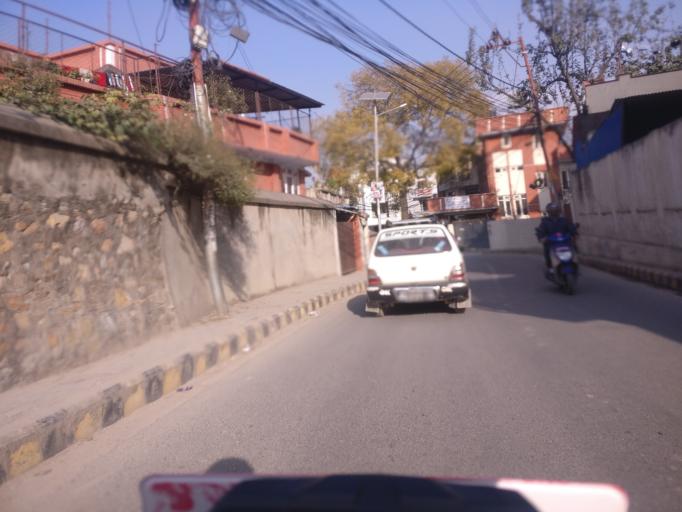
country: NP
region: Central Region
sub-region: Bagmati Zone
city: Patan
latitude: 27.6809
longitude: 85.3244
